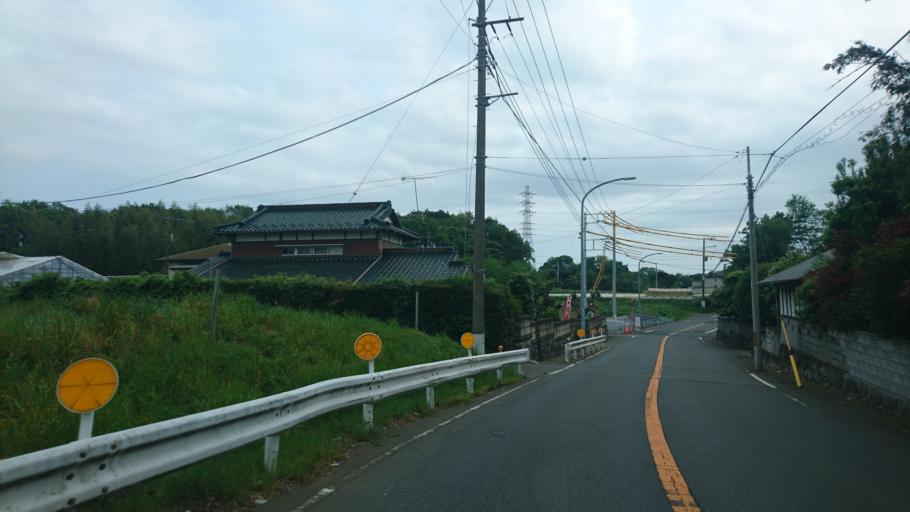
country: JP
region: Kanagawa
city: Fujisawa
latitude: 35.4078
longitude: 139.4790
